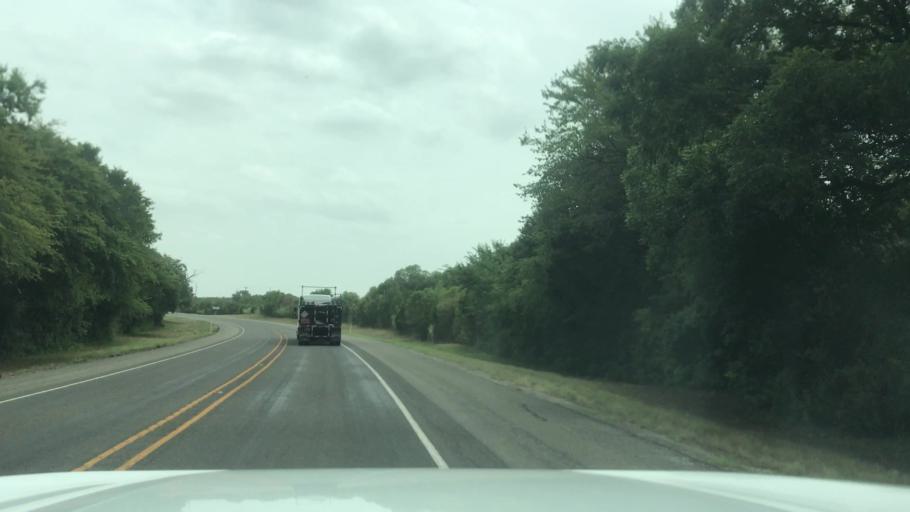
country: US
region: Texas
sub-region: Bosque County
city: Valley Mills
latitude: 31.6775
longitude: -97.5231
